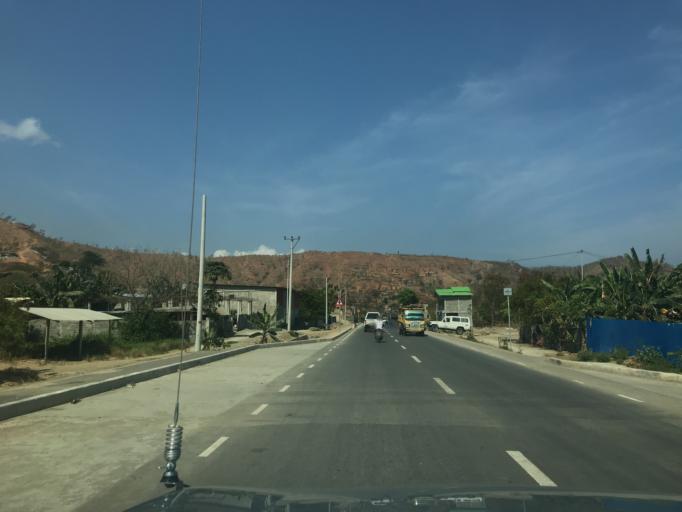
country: TL
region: Dili
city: Dili
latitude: -8.5617
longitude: 125.5312
